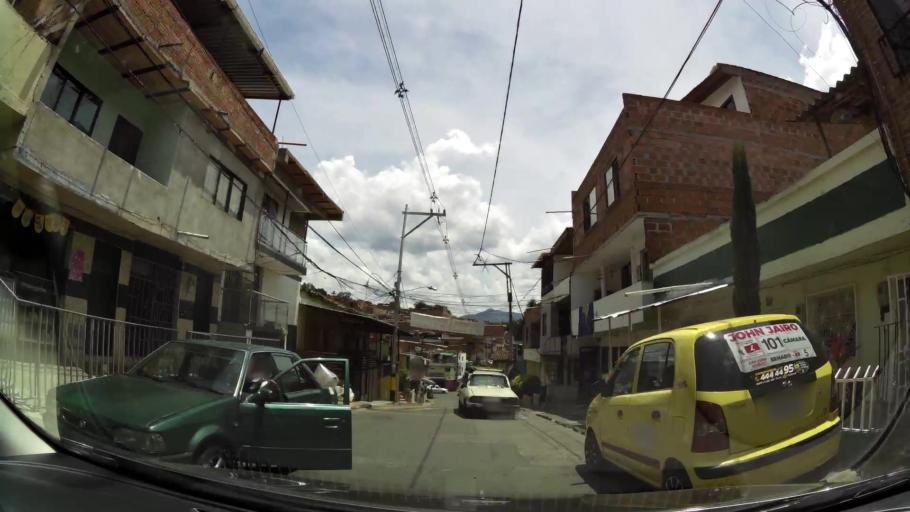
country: CO
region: Antioquia
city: Bello
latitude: 6.3472
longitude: -75.5635
